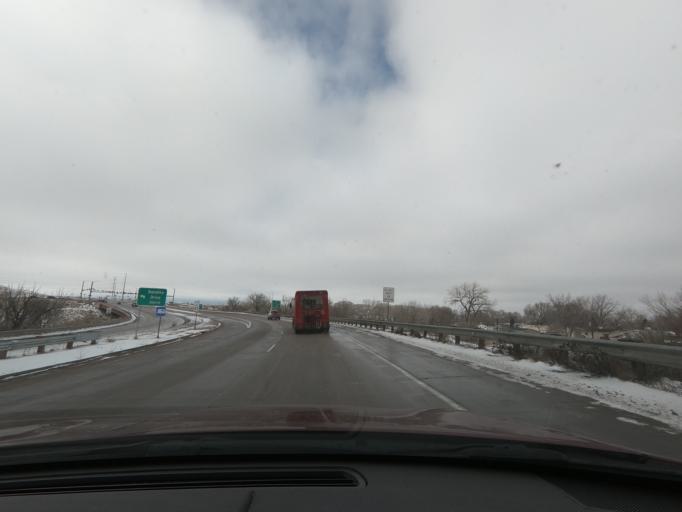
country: US
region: Colorado
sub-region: El Paso County
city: Security-Widefield
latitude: 38.7262
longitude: -104.7284
